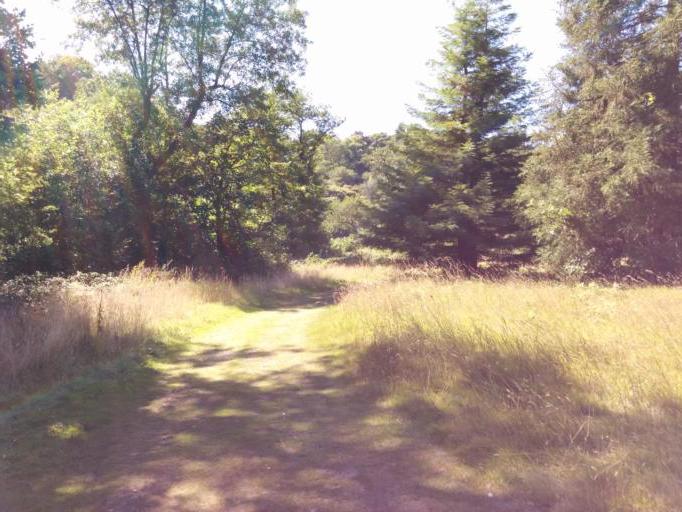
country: GB
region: England
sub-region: Surrey
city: Bramley
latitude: 51.1599
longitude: -0.5762
